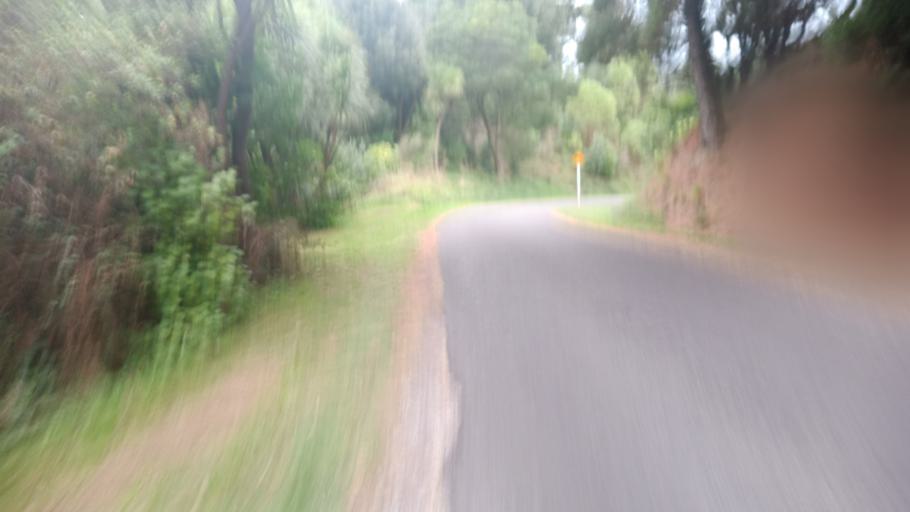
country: NZ
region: Gisborne
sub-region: Gisborne District
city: Gisborne
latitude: -38.6825
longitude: 178.0381
